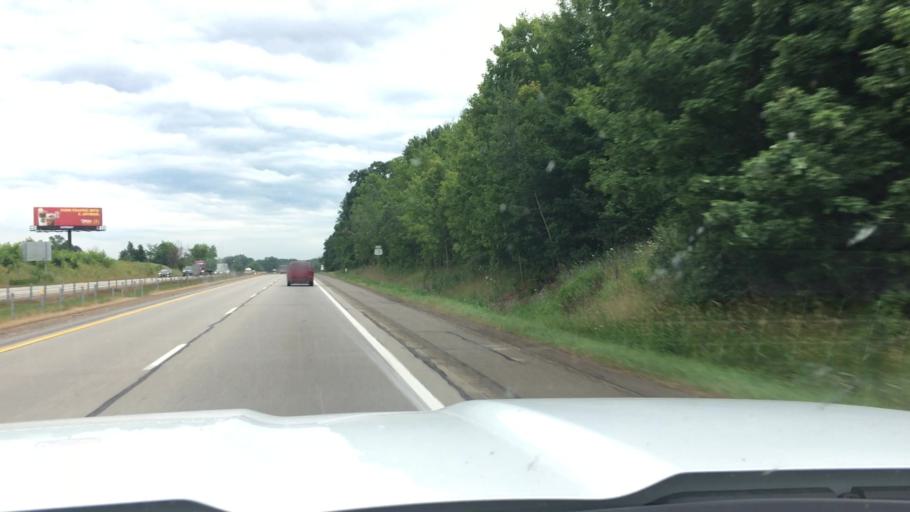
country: US
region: Michigan
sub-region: Allegan County
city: Wayland
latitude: 42.7200
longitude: -85.6694
